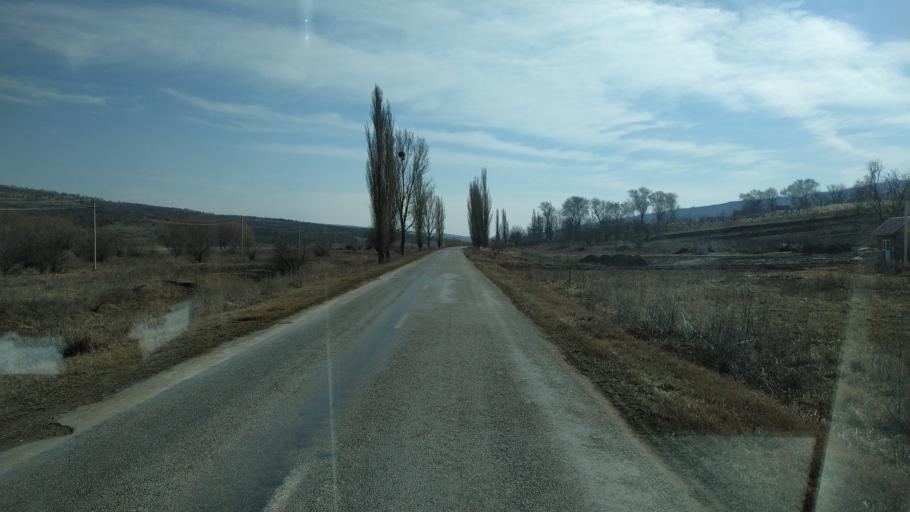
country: MD
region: Nisporeni
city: Nisporeni
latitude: 47.1570
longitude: 28.1063
